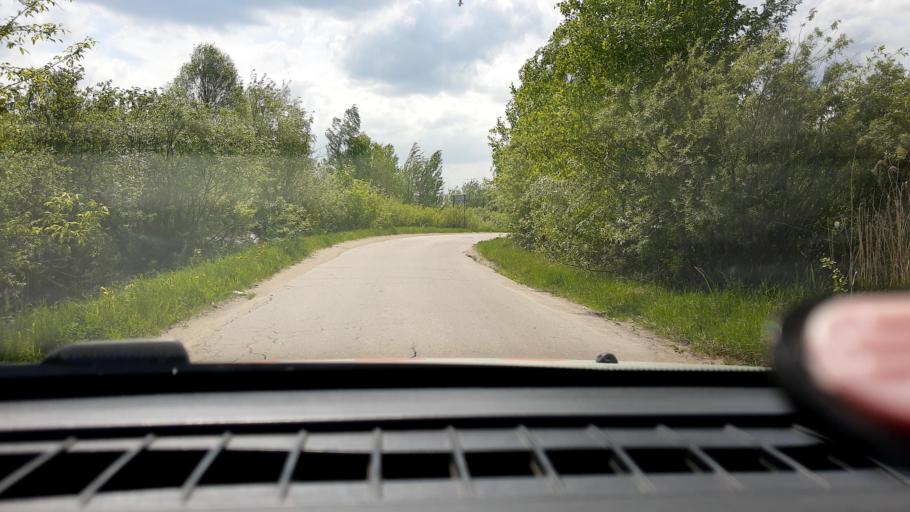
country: RU
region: Nizjnij Novgorod
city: Kstovo
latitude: 56.1363
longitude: 44.1296
